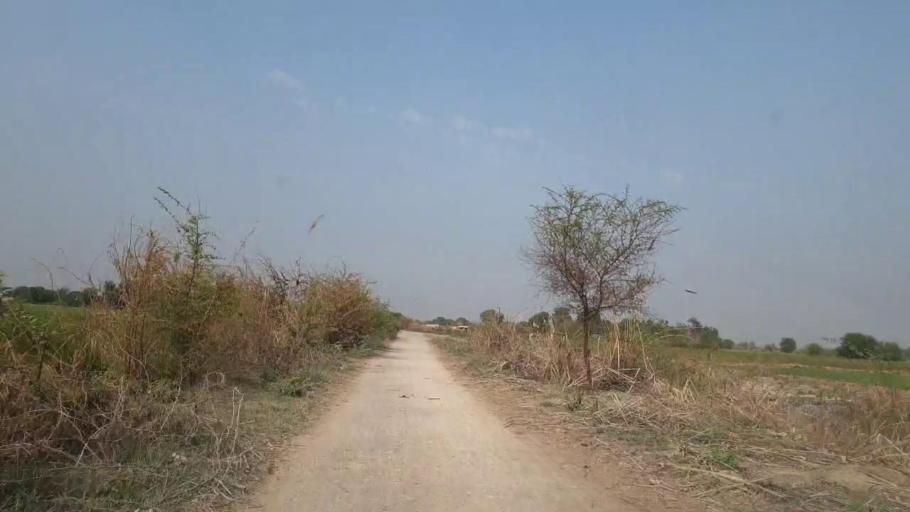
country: PK
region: Sindh
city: Mirpur Khas
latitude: 25.5693
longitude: 69.1522
